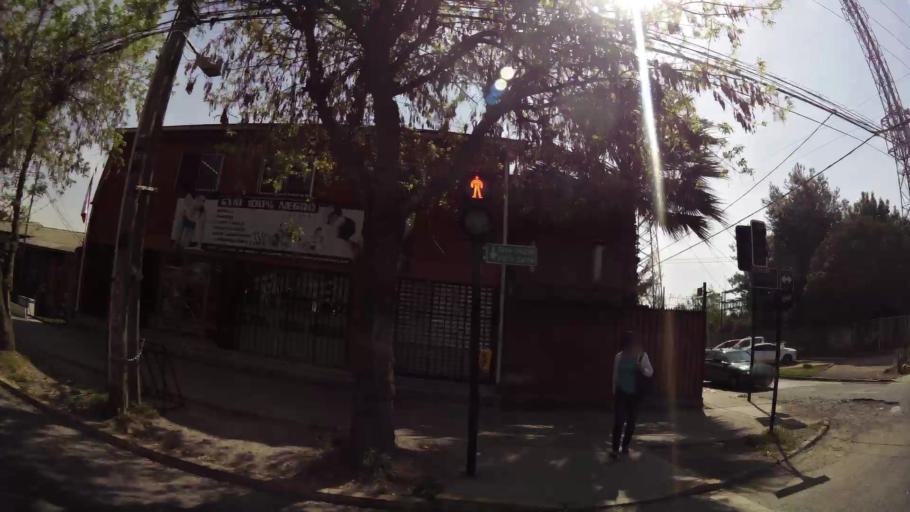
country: CL
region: Santiago Metropolitan
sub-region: Provincia de Santiago
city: Villa Presidente Frei, Nunoa, Santiago, Chile
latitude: -33.5066
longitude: -70.5752
